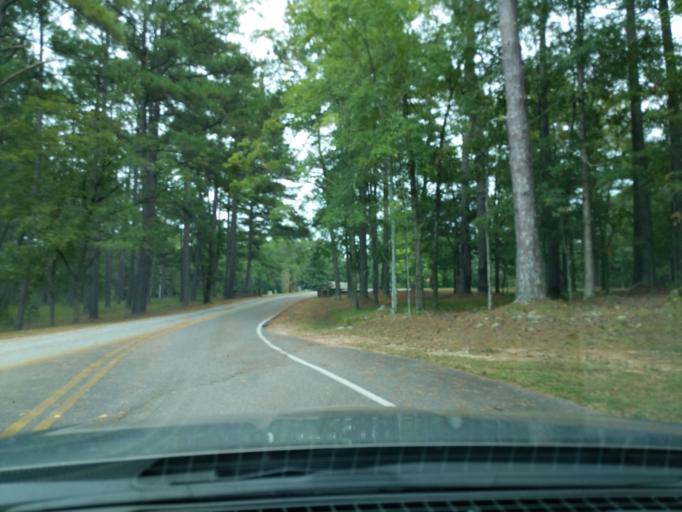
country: US
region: Georgia
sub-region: Columbia County
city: Appling
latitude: 33.6430
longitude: -82.3851
